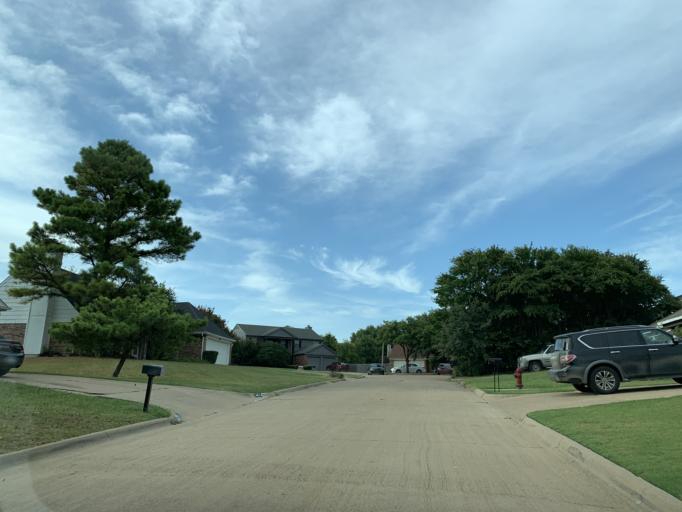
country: US
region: Texas
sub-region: Dallas County
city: Grand Prairie
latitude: 32.6605
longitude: -97.0444
